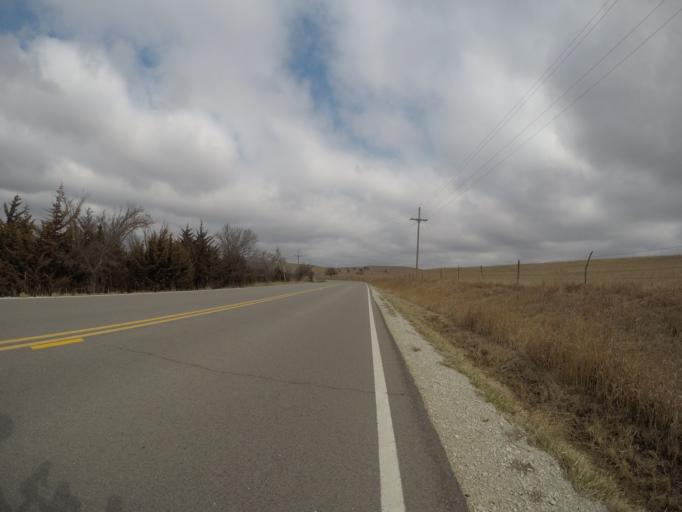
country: US
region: Kansas
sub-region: Pottawatomie County
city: Westmoreland
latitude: 39.4019
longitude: -96.4450
